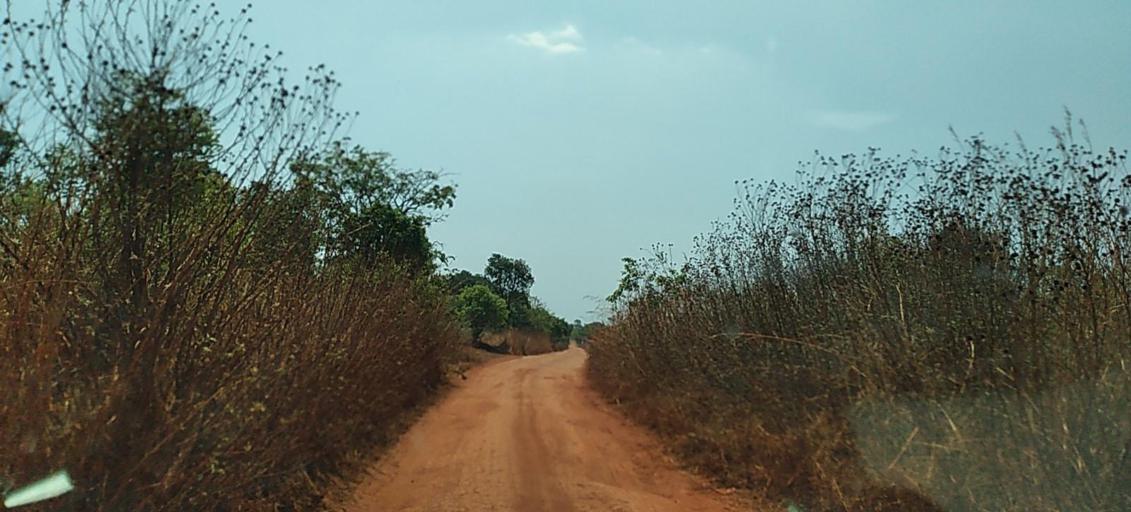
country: ZM
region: North-Western
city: Solwezi
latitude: -12.1321
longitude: 26.3148
